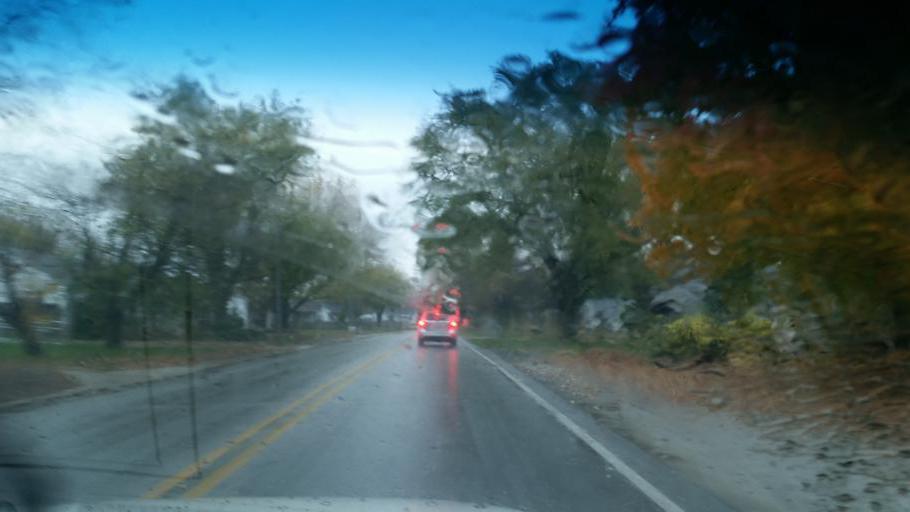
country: US
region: Indiana
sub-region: Howard County
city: Kokomo
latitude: 40.4625
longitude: -86.1288
